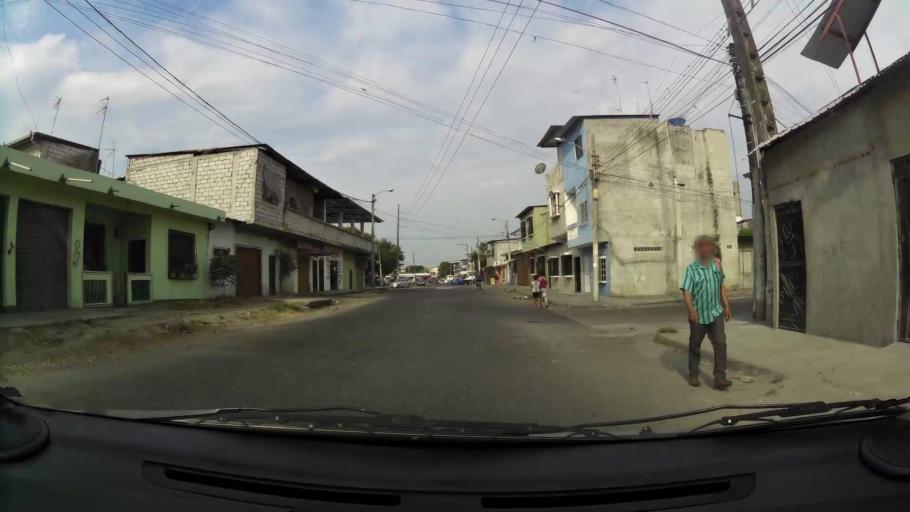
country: EC
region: Guayas
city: Guayaquil
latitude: -2.2509
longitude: -79.9048
